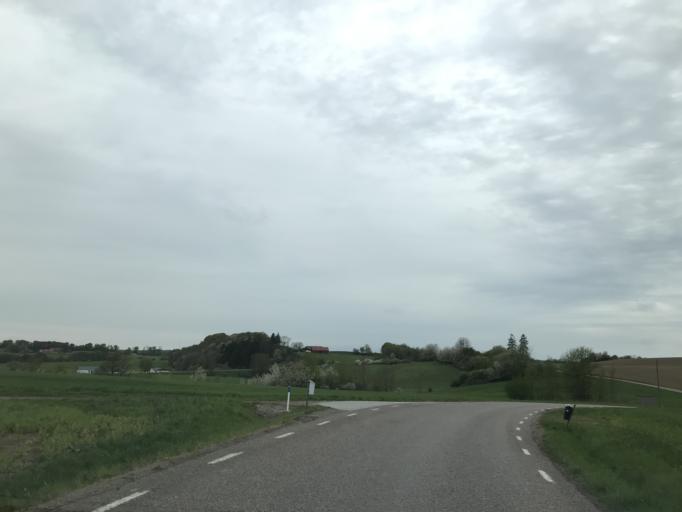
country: SE
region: Skane
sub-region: Trelleborgs Kommun
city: Anderslov
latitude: 55.4781
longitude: 13.3485
